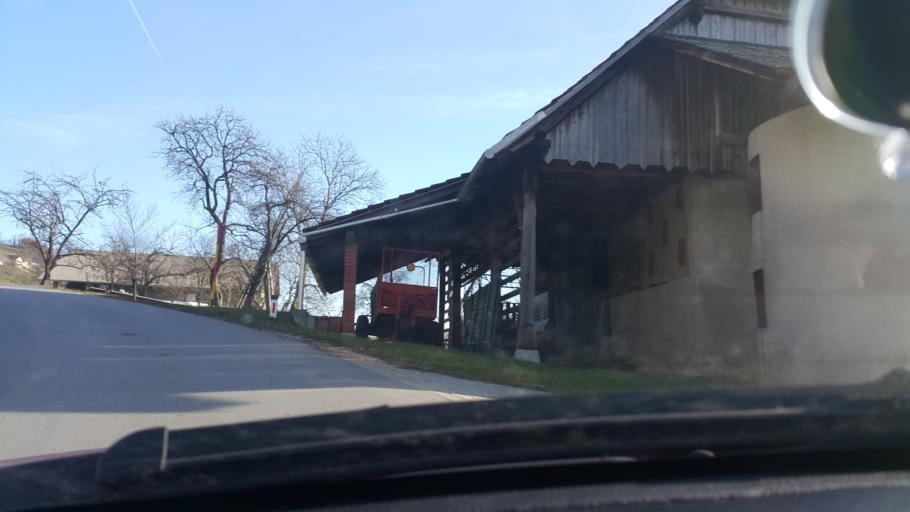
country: SI
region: Velenje
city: Velenje
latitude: 46.3465
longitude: 15.1674
